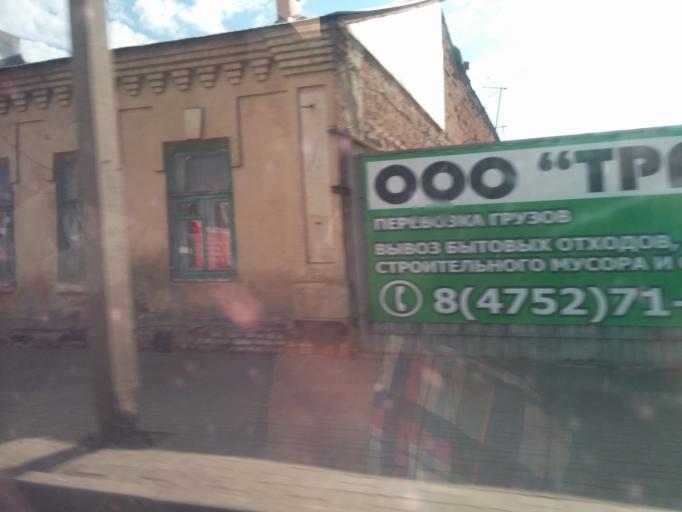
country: RU
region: Tambov
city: Tambov
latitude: 52.7236
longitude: 41.4368
